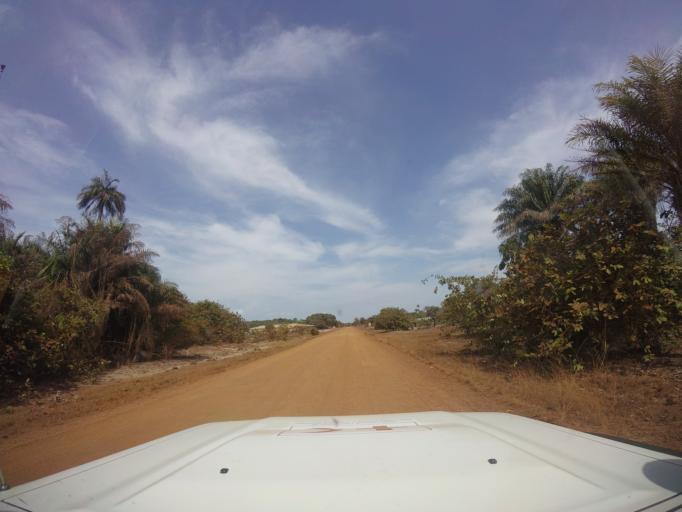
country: LR
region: Grand Cape Mount
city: Robertsport
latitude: 6.6915
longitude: -11.2702
